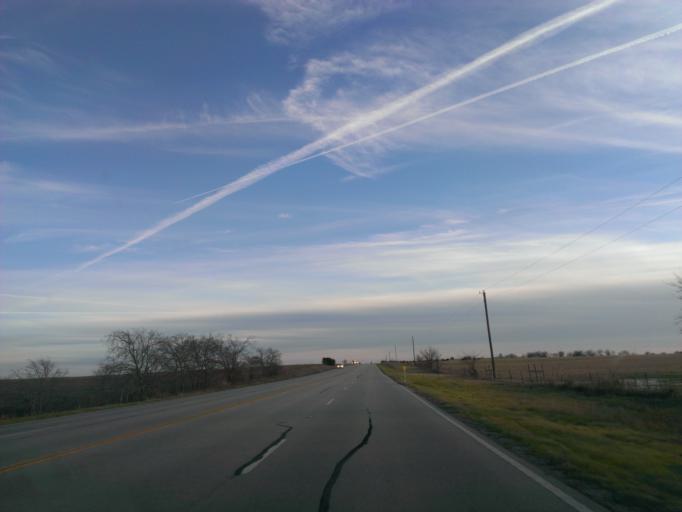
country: US
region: Texas
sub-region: Williamson County
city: Florence
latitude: 30.8672
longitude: -97.9146
